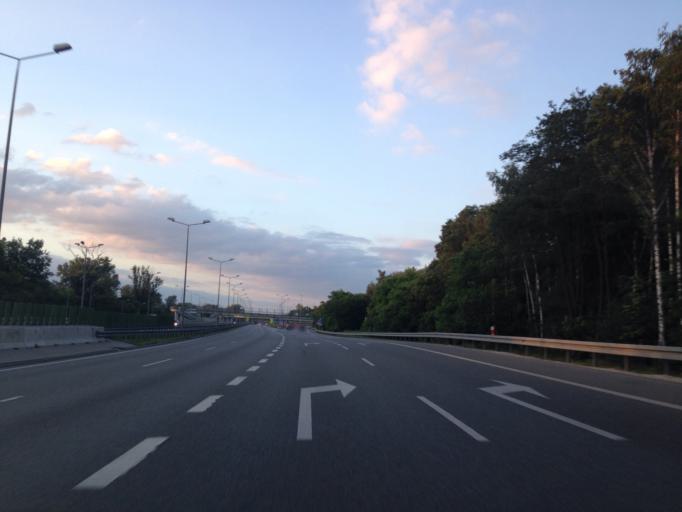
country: PL
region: Masovian Voivodeship
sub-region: Warszawa
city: Bemowo
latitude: 52.2529
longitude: 20.9443
